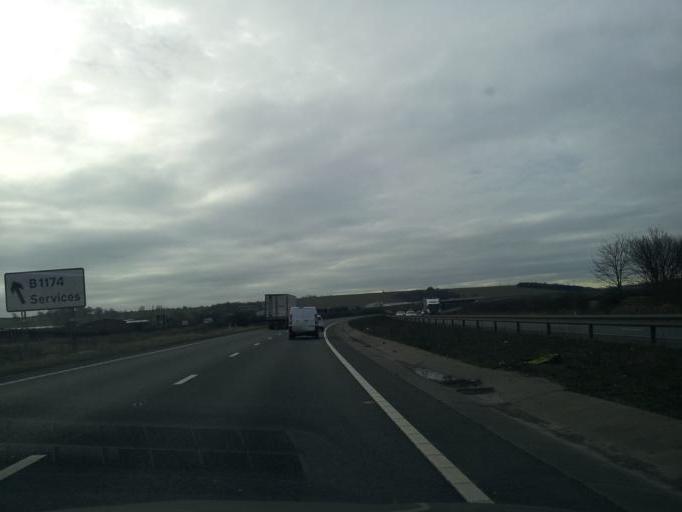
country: GB
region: England
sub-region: Lincolnshire
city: Great Gonerby
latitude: 52.9549
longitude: -0.6837
